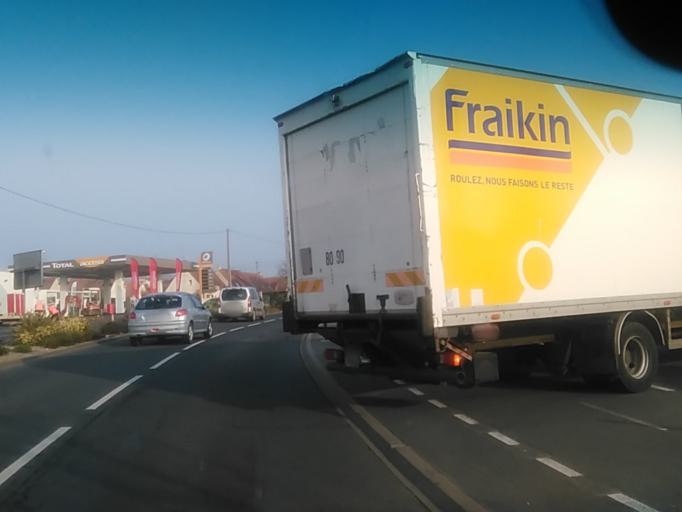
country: FR
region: Lower Normandy
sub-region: Departement du Calvados
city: Louvigny
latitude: 49.1723
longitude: -0.3887
